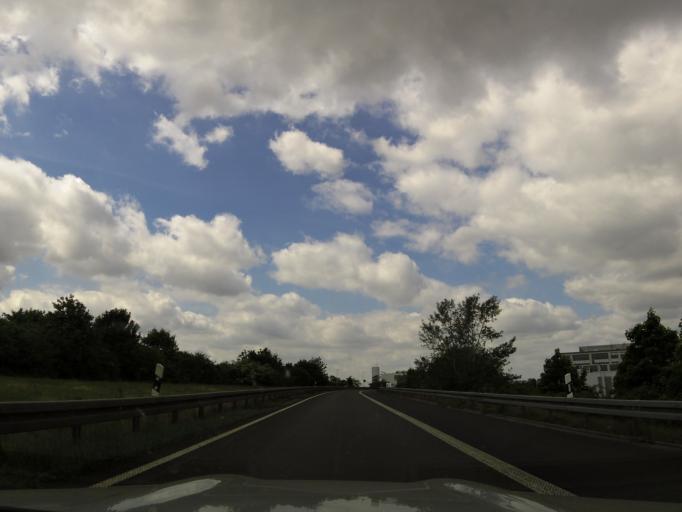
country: DE
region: Hesse
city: Niederrad
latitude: 50.0538
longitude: 8.6008
